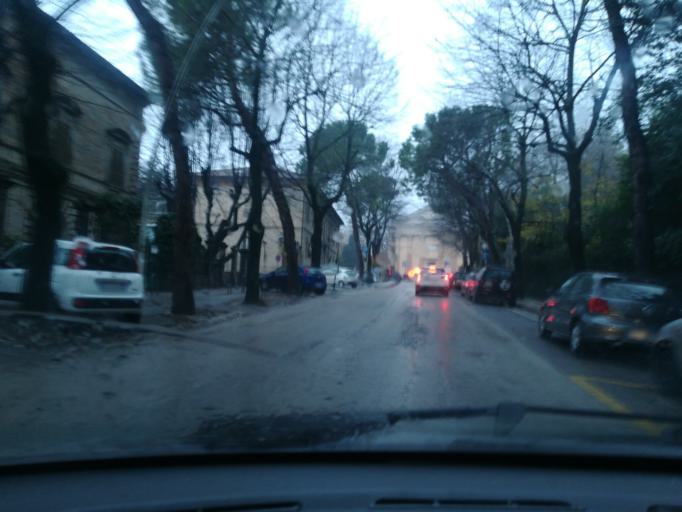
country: IT
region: The Marches
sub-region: Provincia di Macerata
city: Macerata
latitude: 43.2999
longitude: 13.4376
